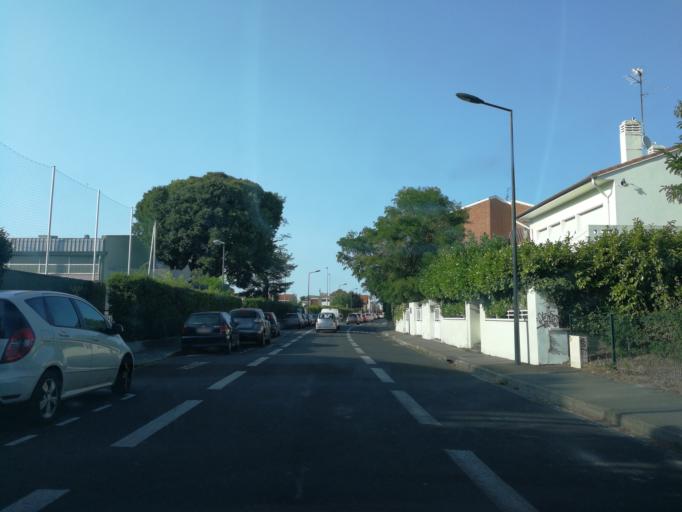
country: FR
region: Midi-Pyrenees
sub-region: Departement de la Haute-Garonne
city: Toulouse
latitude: 43.6240
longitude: 1.4368
